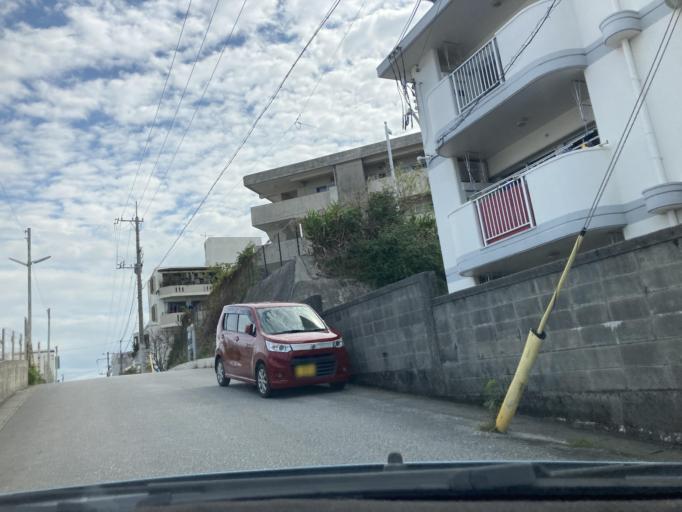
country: JP
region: Okinawa
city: Tomigusuku
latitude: 26.1982
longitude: 127.6935
